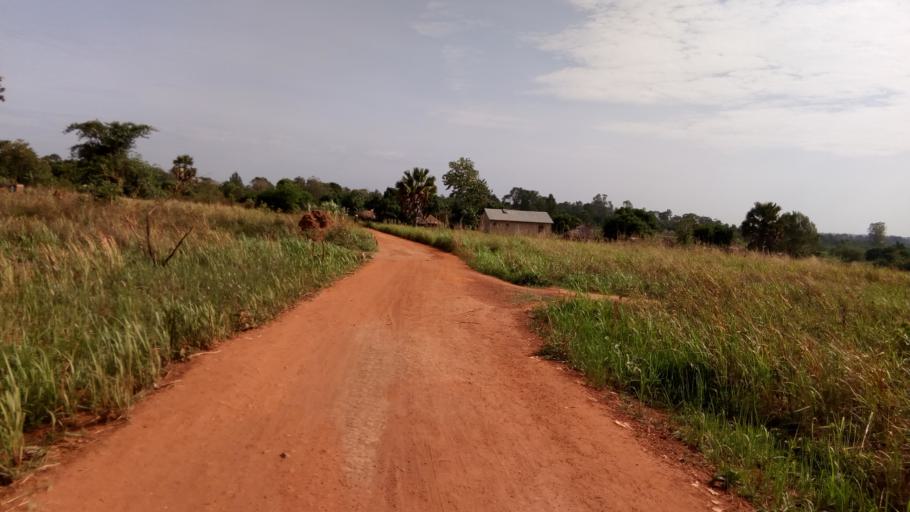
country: UG
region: Northern Region
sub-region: Gulu District
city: Gulu
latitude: 2.7993
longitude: 32.3233
